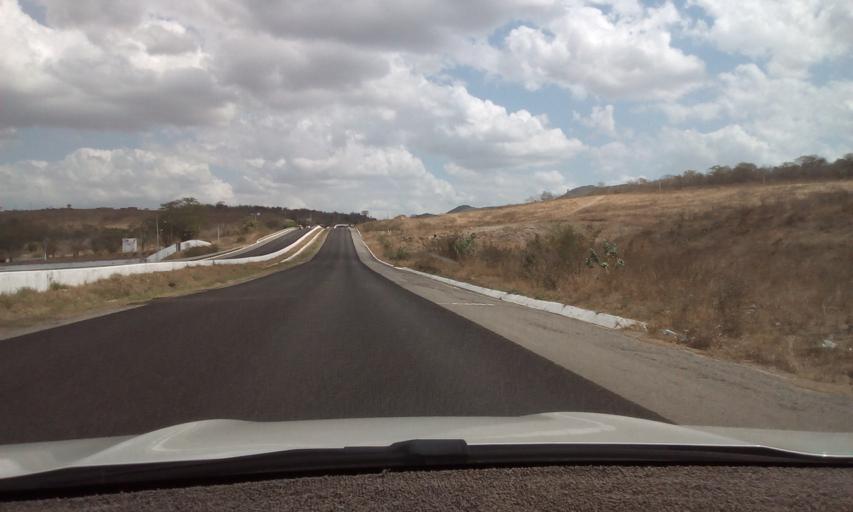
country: BR
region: Pernambuco
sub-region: Toritama
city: Toritama
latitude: -8.0620
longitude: -36.0476
